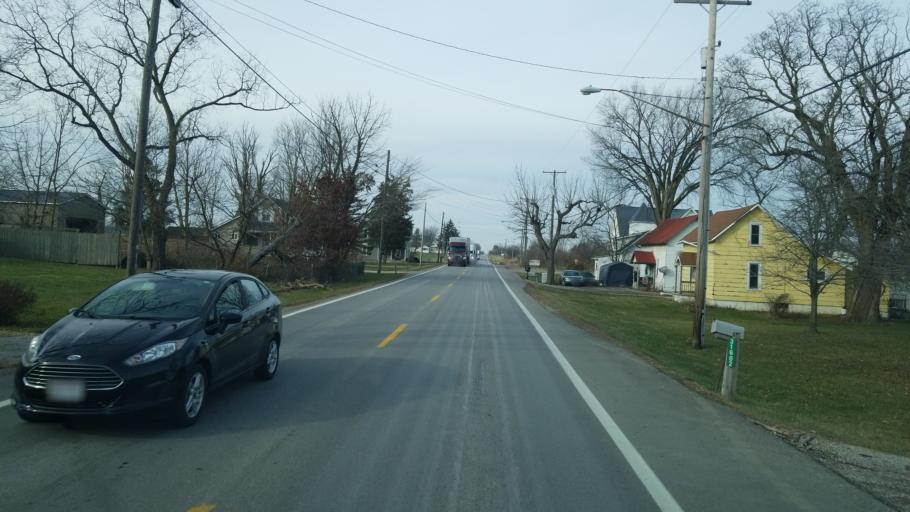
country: US
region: Ohio
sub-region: Union County
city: Richwood
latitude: 40.4552
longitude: -83.4567
